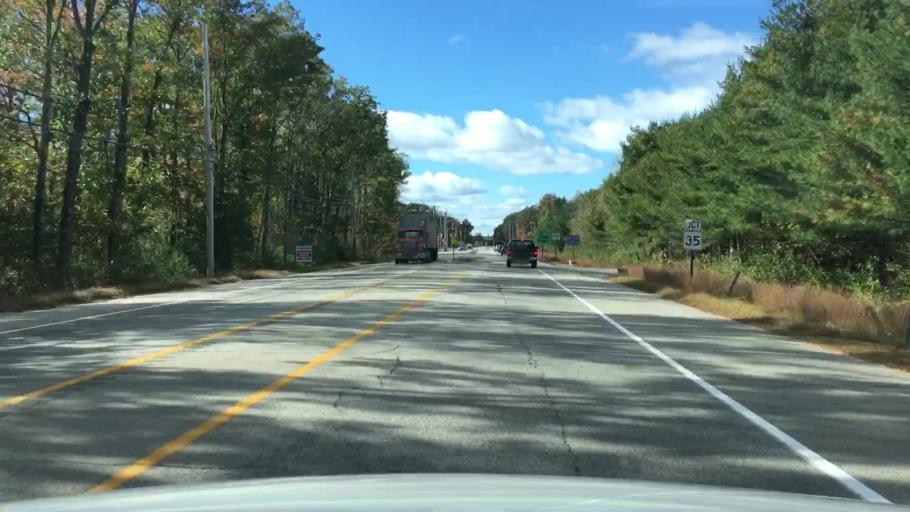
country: US
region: Maine
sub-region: York County
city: West Kennebunk
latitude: 43.4796
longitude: -70.6008
